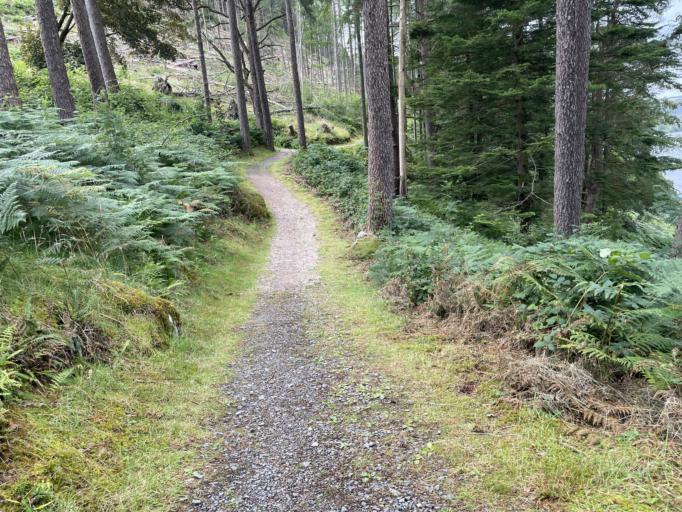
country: GB
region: Scotland
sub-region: Dumfries and Galloway
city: Newton Stewart
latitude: 55.0889
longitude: -4.4710
